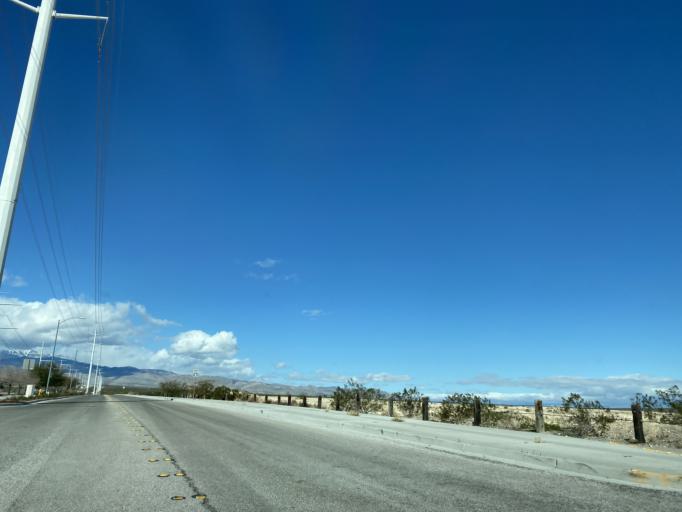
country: US
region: Nevada
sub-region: Clark County
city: North Las Vegas
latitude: 36.3359
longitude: -115.2741
